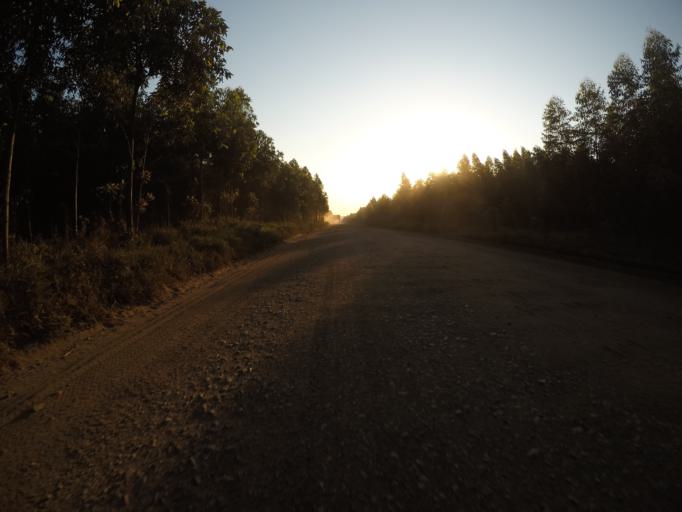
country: ZA
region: KwaZulu-Natal
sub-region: uThungulu District Municipality
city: KwaMbonambi
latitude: -28.6680
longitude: 32.0728
